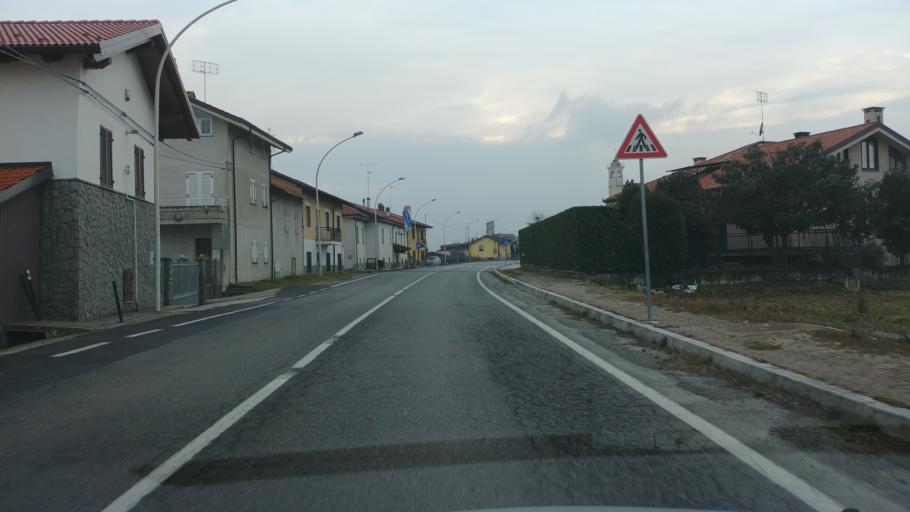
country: IT
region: Piedmont
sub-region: Provincia di Cuneo
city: Castelletto Stura
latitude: 44.4345
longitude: 7.5907
